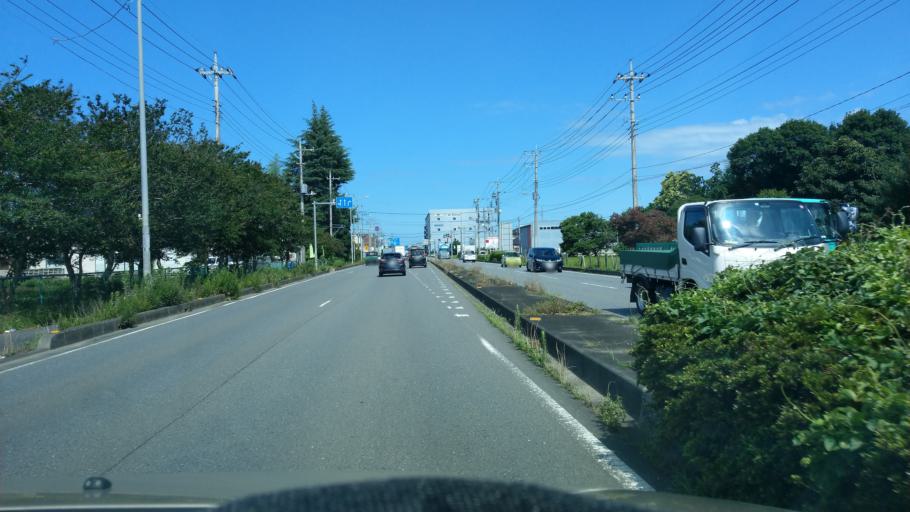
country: JP
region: Saitama
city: Sakado
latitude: 36.0326
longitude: 139.3679
